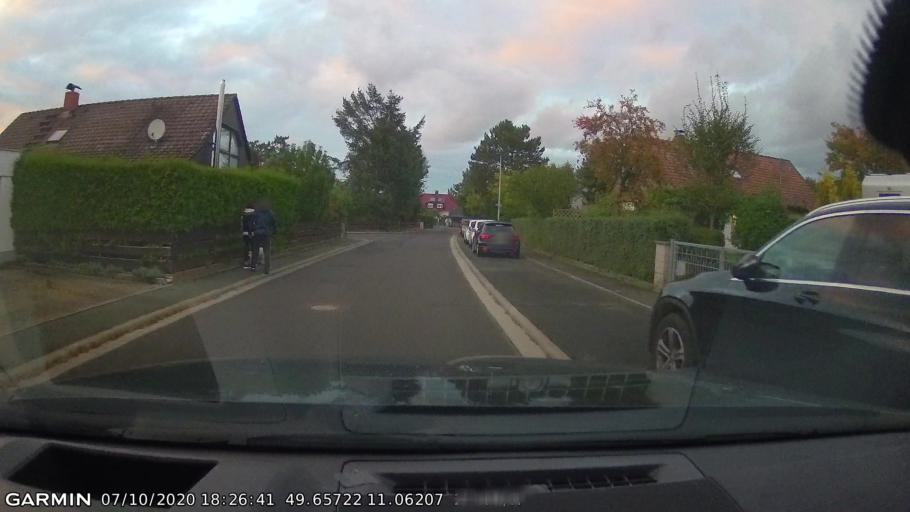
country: DE
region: Bavaria
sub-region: Upper Franconia
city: Poxdorf
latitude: 49.6571
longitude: 11.0623
